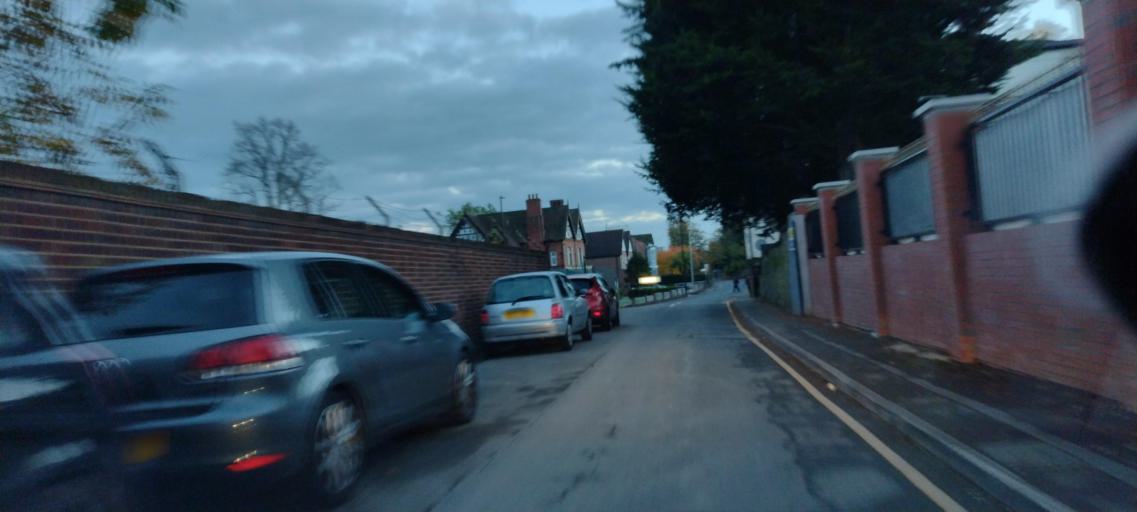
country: GB
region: England
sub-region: Coventry
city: Coventry
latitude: 52.4165
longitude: -1.5148
